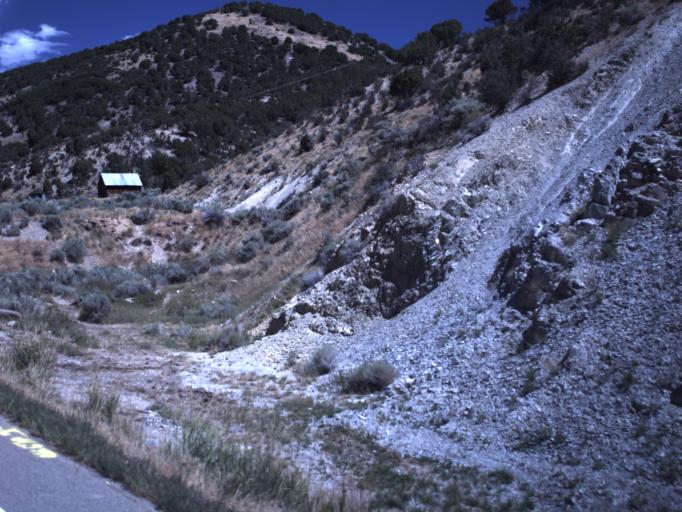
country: US
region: Utah
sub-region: Summit County
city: Oakley
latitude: 40.7347
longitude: -111.3493
